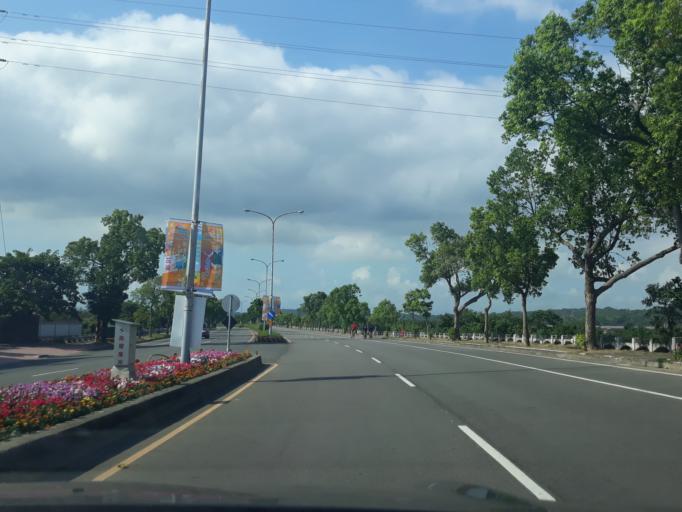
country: TW
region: Taiwan
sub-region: Miaoli
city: Miaoli
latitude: 24.5819
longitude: 120.8431
